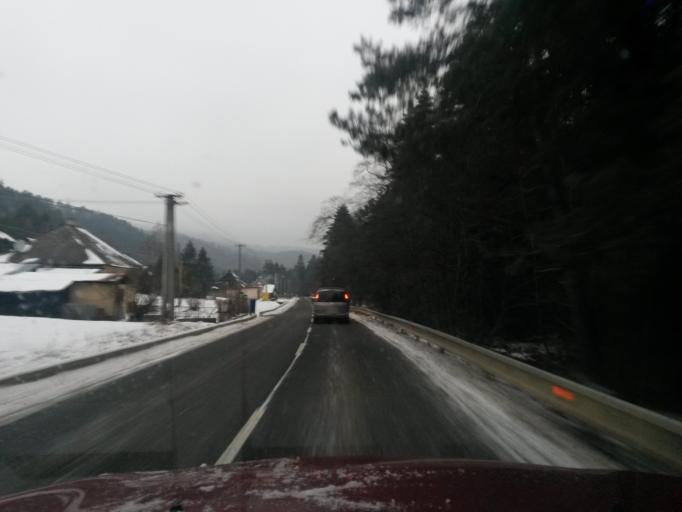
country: SK
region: Kosicky
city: Medzev
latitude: 48.7512
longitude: 20.7777
